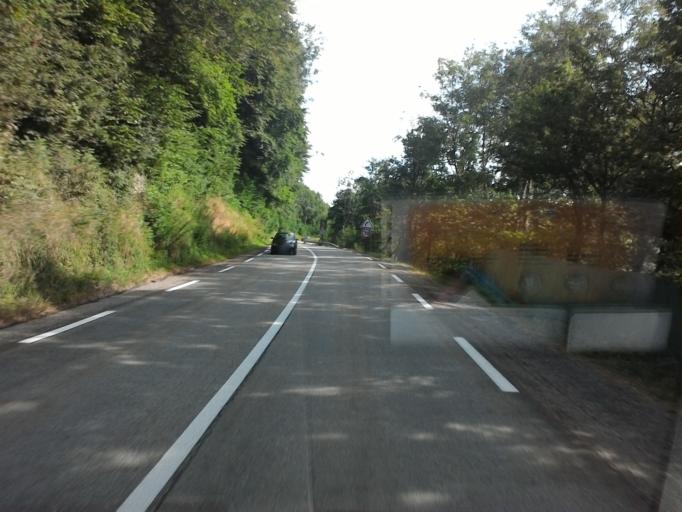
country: FR
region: Rhone-Alpes
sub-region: Departement de l'Isere
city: Notre-Dame-de-Mesage
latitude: 45.0148
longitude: 5.7745
